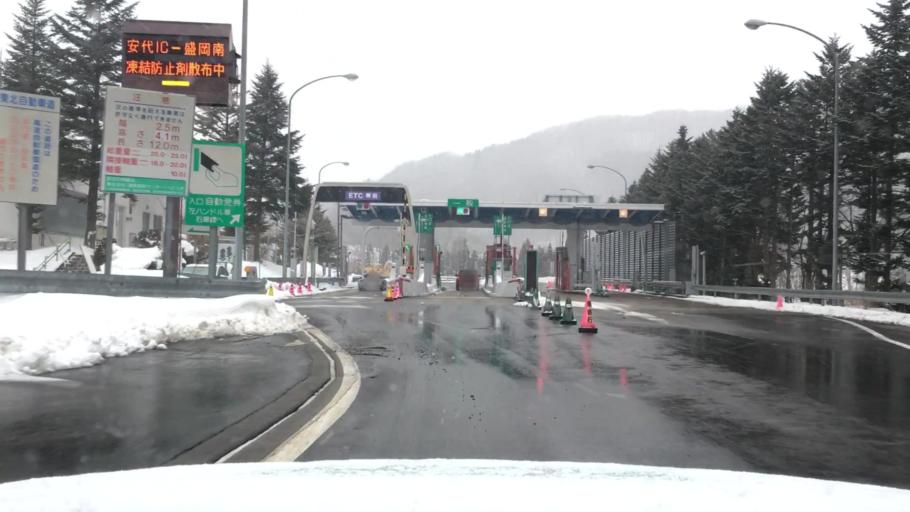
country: JP
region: Iwate
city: Ichinohe
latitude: 40.1103
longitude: 141.0512
